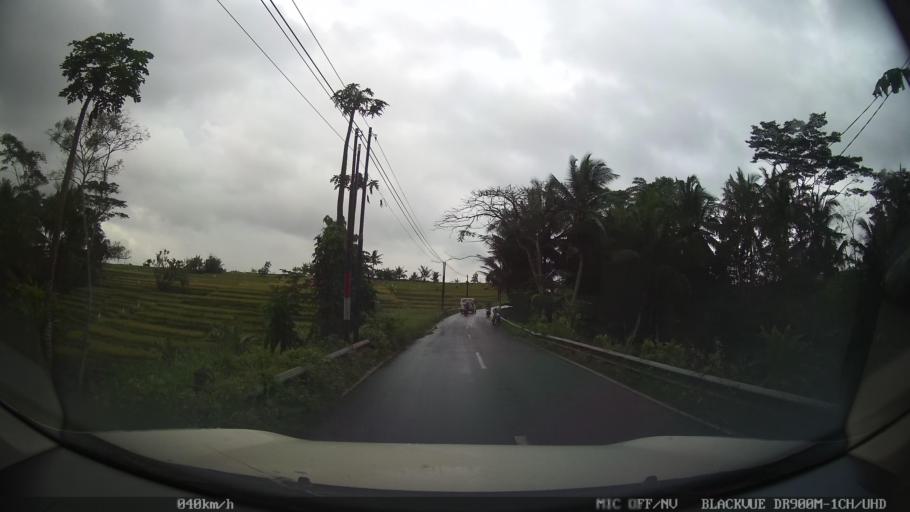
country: ID
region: Bali
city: Banjar Teguan
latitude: -8.5048
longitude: 115.2281
